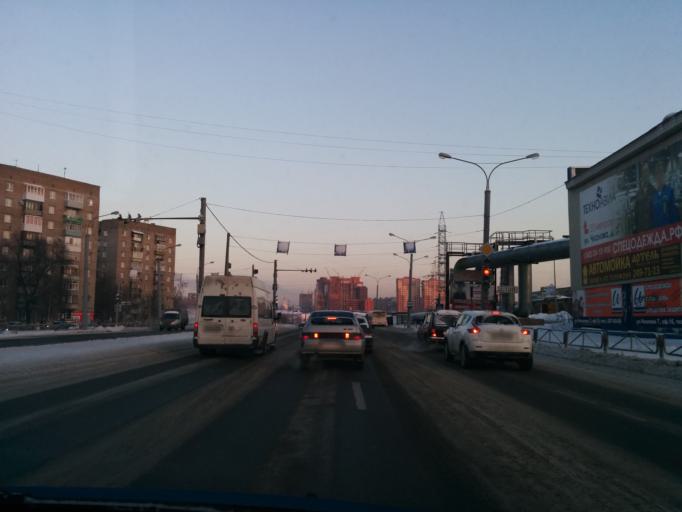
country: RU
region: Perm
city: Perm
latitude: 57.9855
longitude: 56.2670
